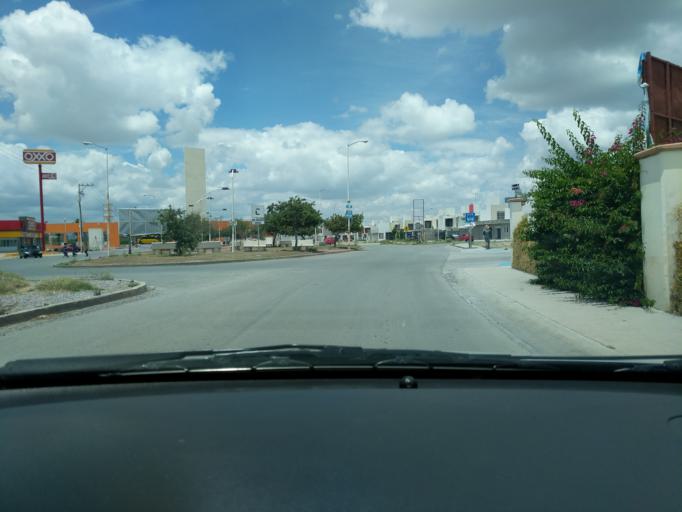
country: MX
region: San Luis Potosi
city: Soledad Diez Gutierrez
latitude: 22.2155
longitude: -100.9373
